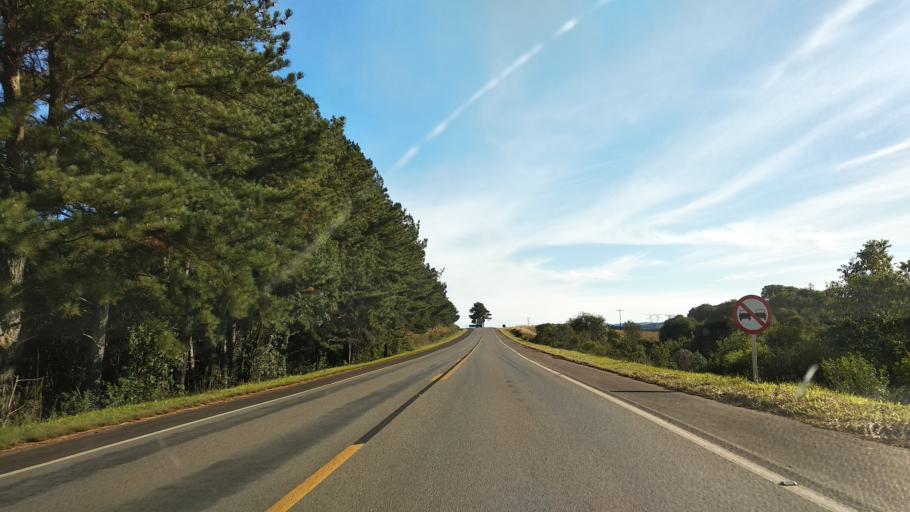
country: BR
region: Santa Catarina
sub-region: Celso Ramos
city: Celso Ramos
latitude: -27.5317
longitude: -51.3941
